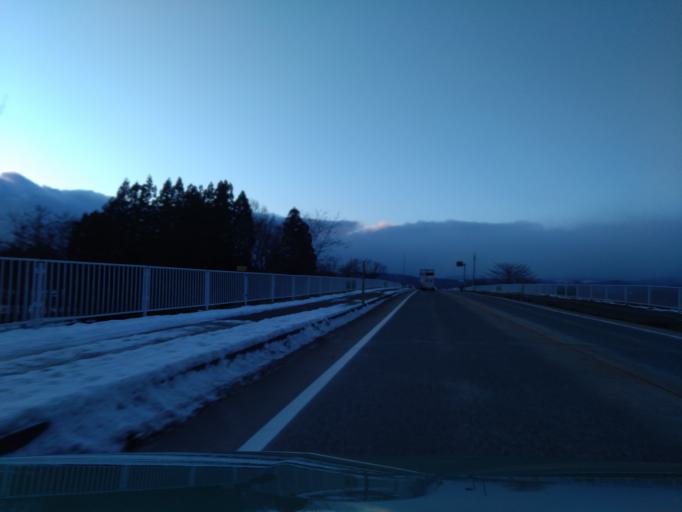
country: JP
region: Iwate
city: Shizukuishi
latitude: 39.6904
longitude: 140.9887
